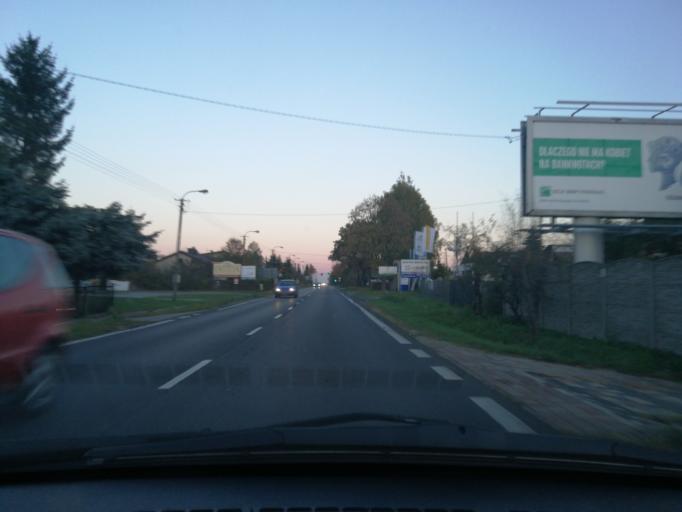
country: PL
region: Lodz Voivodeship
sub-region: Powiat lodzki wschodni
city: Andrespol
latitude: 51.7950
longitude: 19.5717
